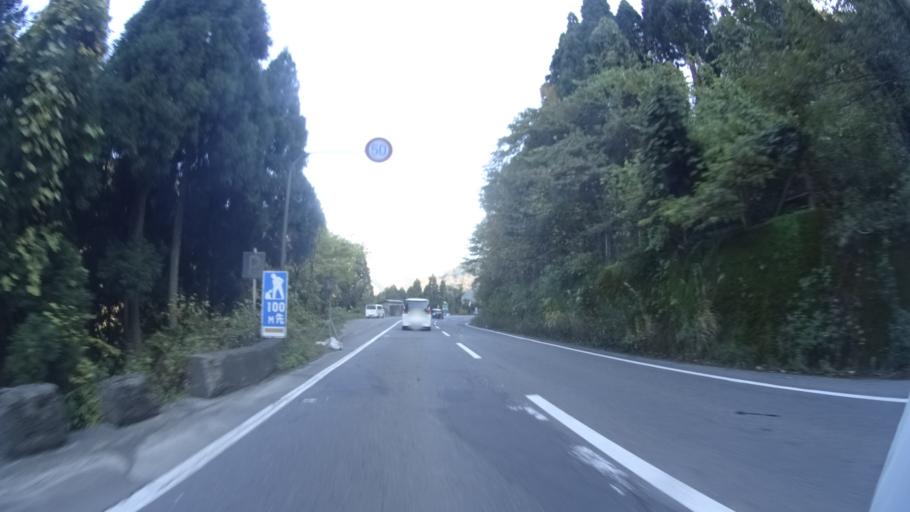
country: JP
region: Fukui
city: Ono
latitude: 35.9682
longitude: 136.5746
